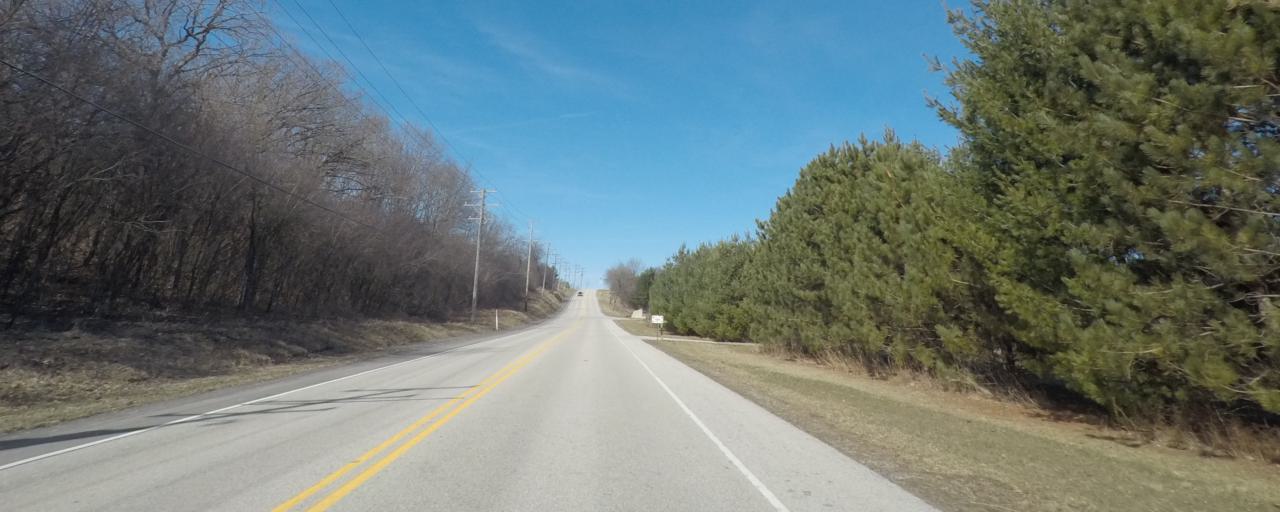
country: US
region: Wisconsin
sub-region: Waukesha County
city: Merton
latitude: 43.1492
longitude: -88.3266
